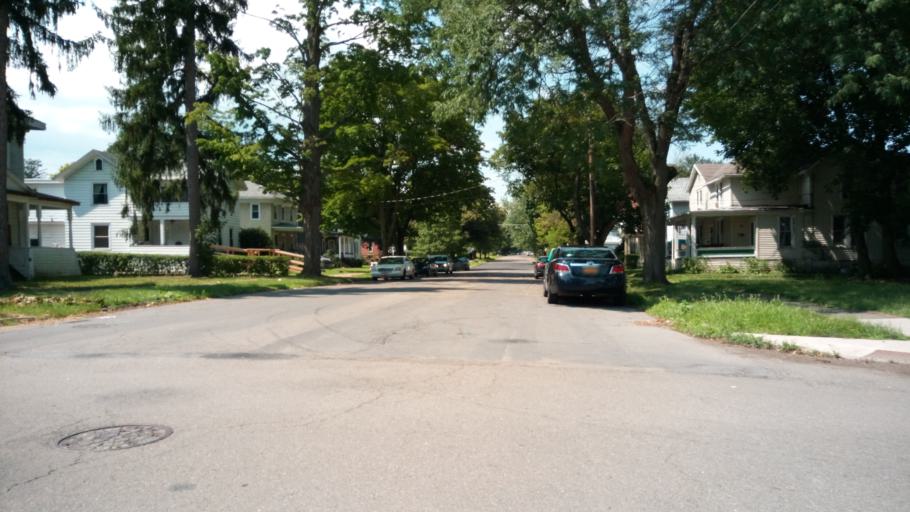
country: US
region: New York
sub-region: Chemung County
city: Elmira
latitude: 42.0872
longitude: -76.8202
